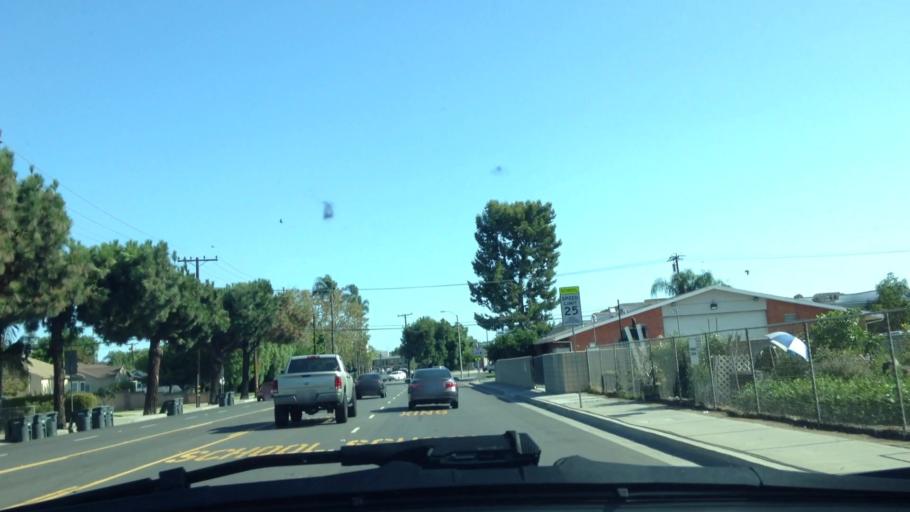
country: US
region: California
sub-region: Orange County
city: Orange
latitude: 33.7907
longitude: -117.8666
